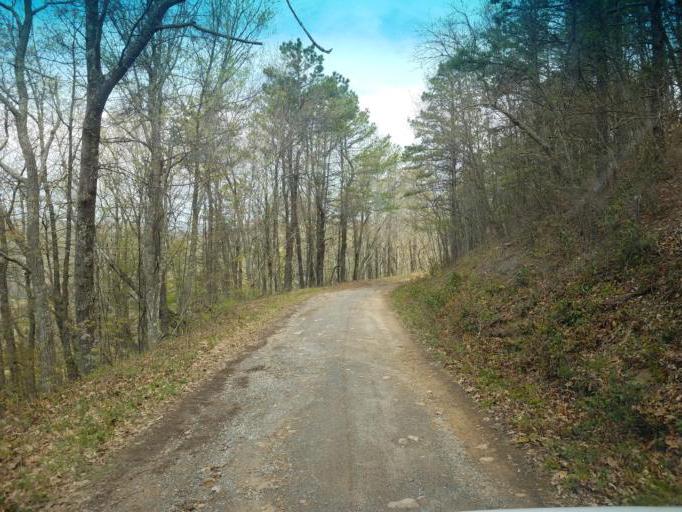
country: US
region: Virginia
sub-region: Smyth County
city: Marion
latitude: 36.7894
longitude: -81.4712
